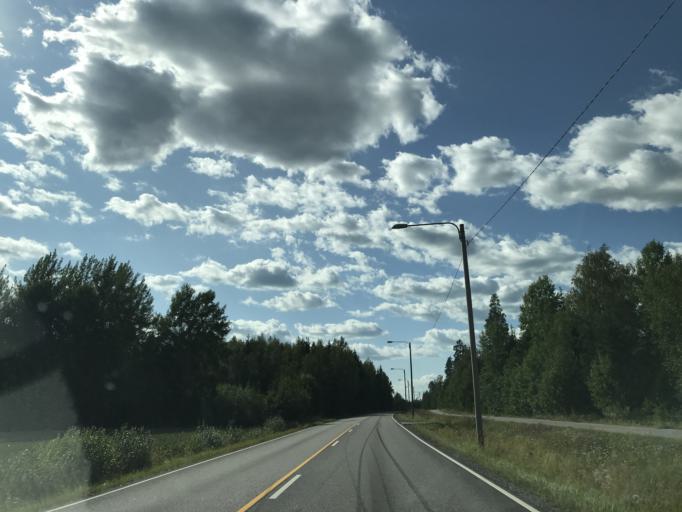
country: FI
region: Uusimaa
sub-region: Helsinki
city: Nurmijaervi
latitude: 60.4340
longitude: 24.8448
